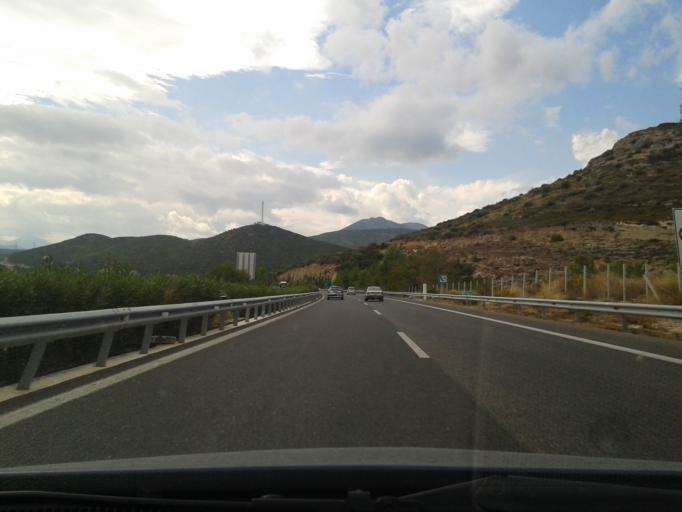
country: GR
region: Peloponnese
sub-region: Nomos Korinthias
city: Nemea
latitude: 37.8027
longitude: 22.7269
